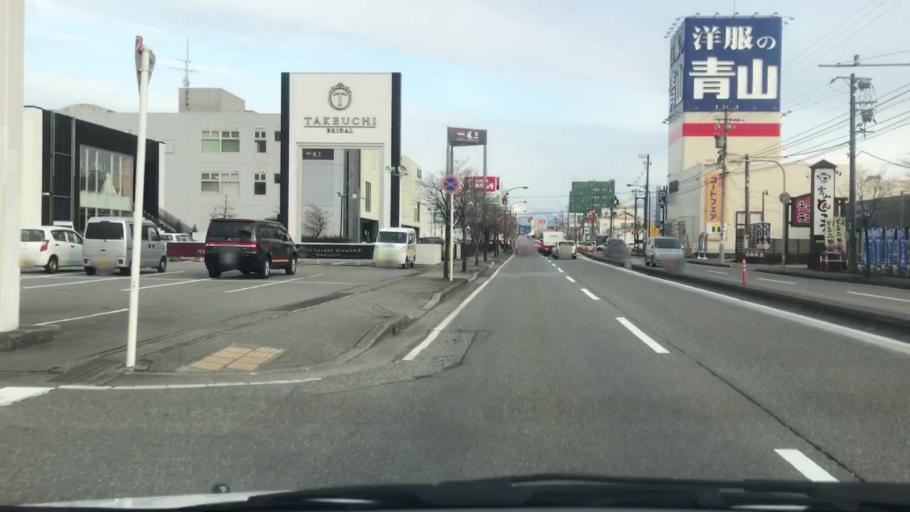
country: JP
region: Toyama
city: Toyama-shi
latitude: 36.6669
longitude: 137.2049
